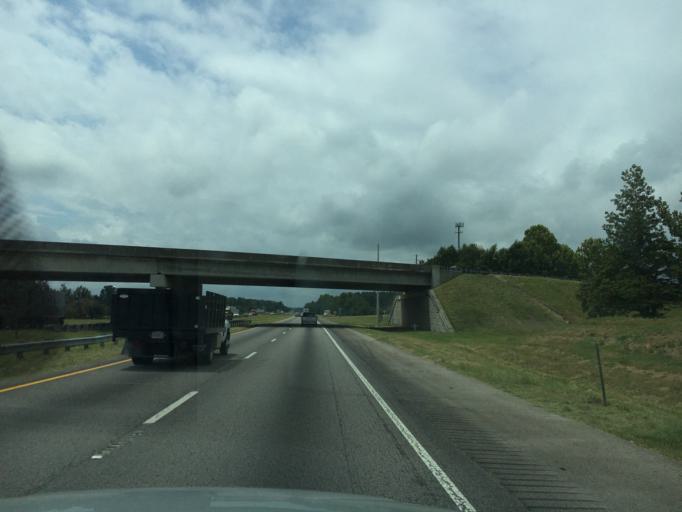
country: US
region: Georgia
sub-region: Jackson County
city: Jefferson
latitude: 34.1870
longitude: -83.5930
